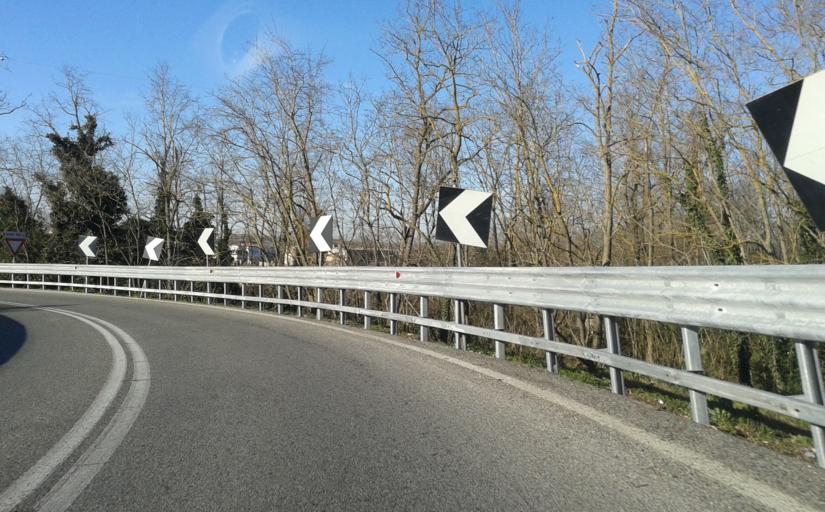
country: IT
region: Tuscany
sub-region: Provincia di Livorno
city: Livorno
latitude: 43.5843
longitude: 10.3500
